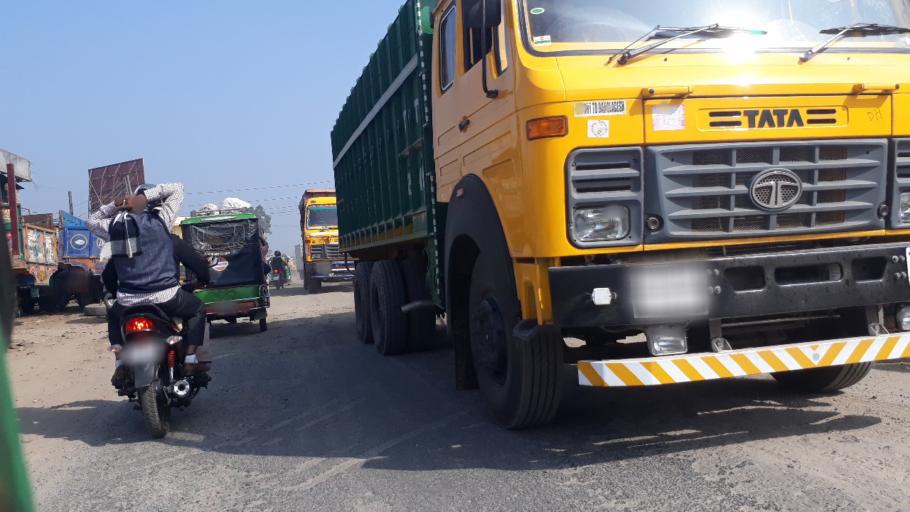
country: BD
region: Khulna
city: Kushtia
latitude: 23.8815
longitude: 89.0944
